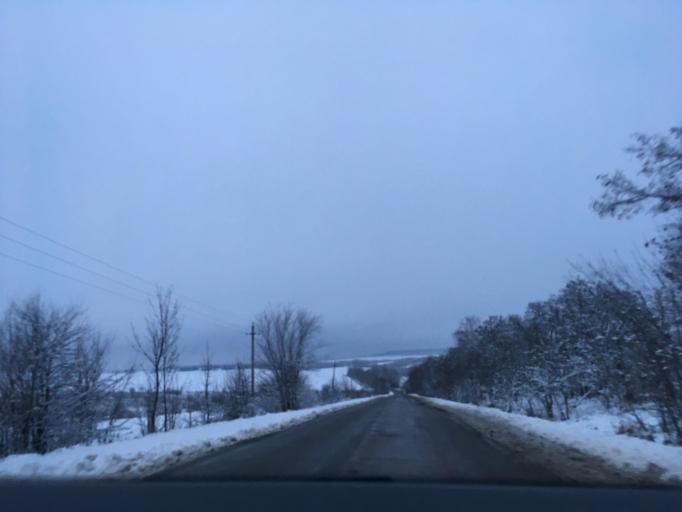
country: RU
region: Voronezj
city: Verkhniy Mamon
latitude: 50.0509
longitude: 40.2456
